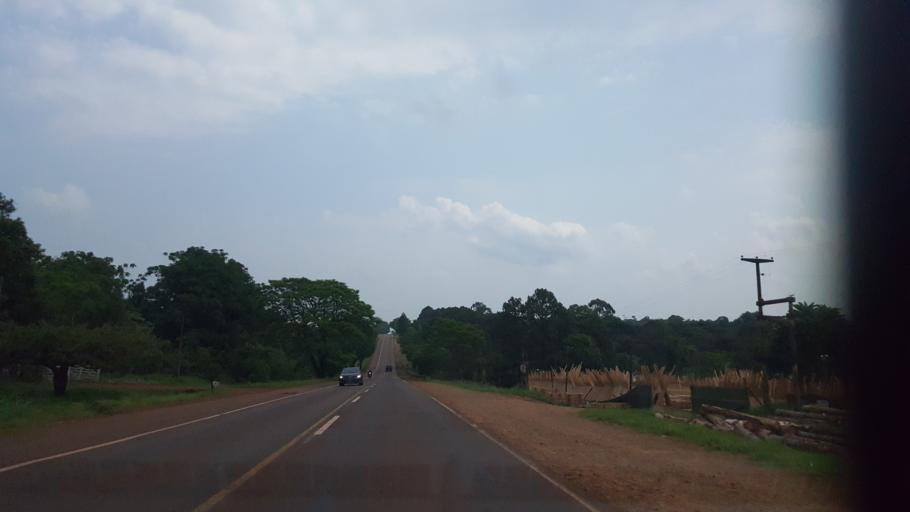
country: AR
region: Misiones
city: Jardin America
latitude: -27.0564
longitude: -55.2550
